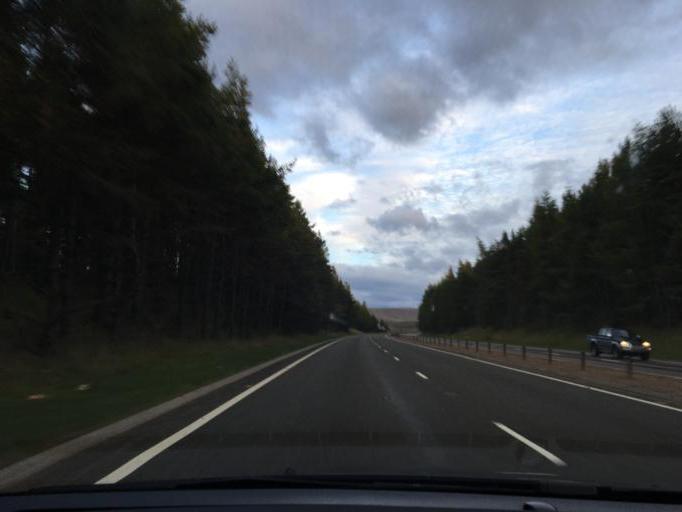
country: GB
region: Scotland
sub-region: Highland
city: Aviemore
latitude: 57.3397
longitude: -3.9882
